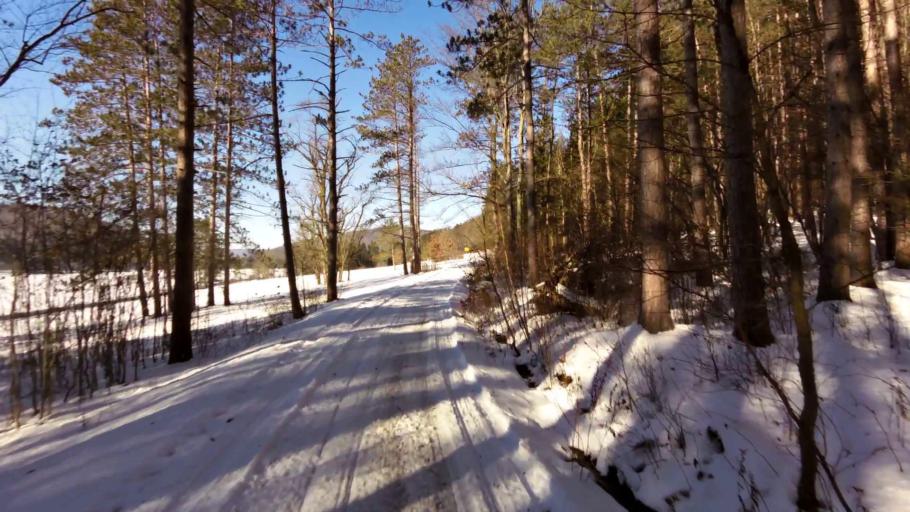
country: US
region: New York
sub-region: Cattaraugus County
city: Salamanca
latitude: 42.1025
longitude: -78.7376
